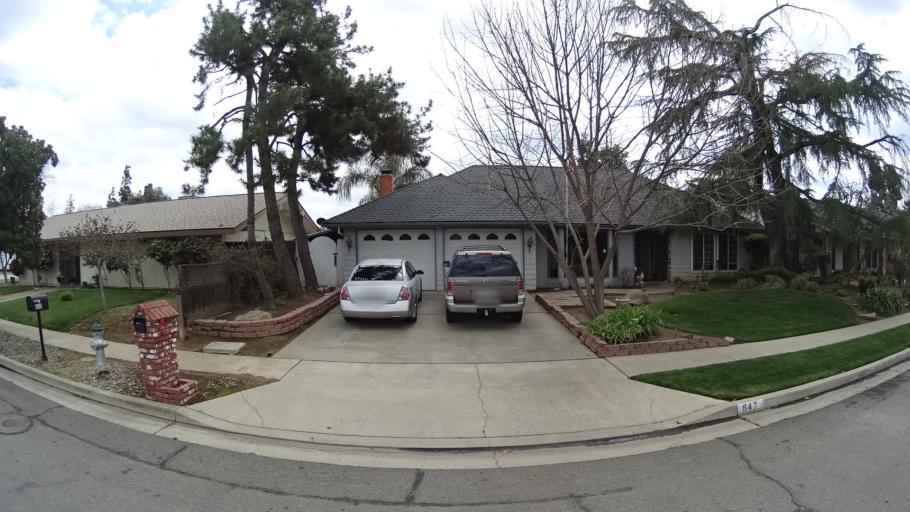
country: US
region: California
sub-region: Fresno County
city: Fresno
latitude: 36.8349
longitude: -119.8049
